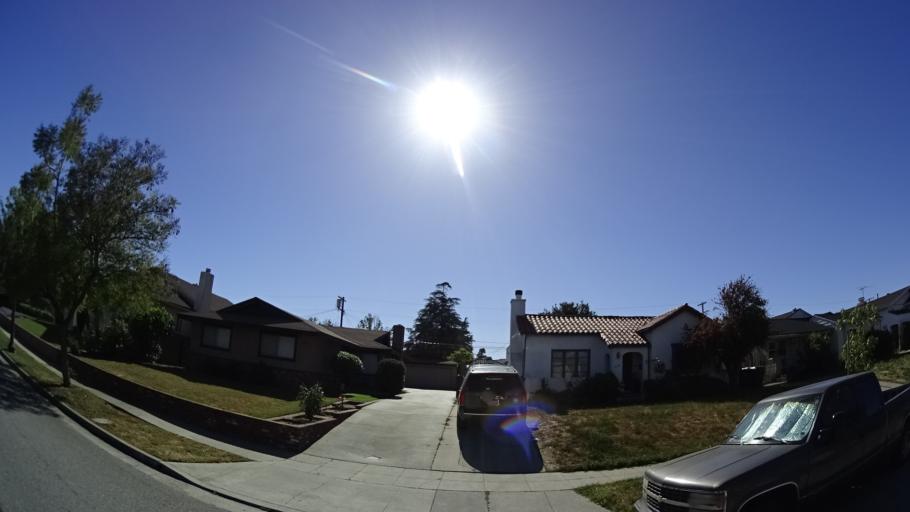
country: US
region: California
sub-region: Los Angeles County
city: Monterey Park
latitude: 34.0743
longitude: -118.1487
